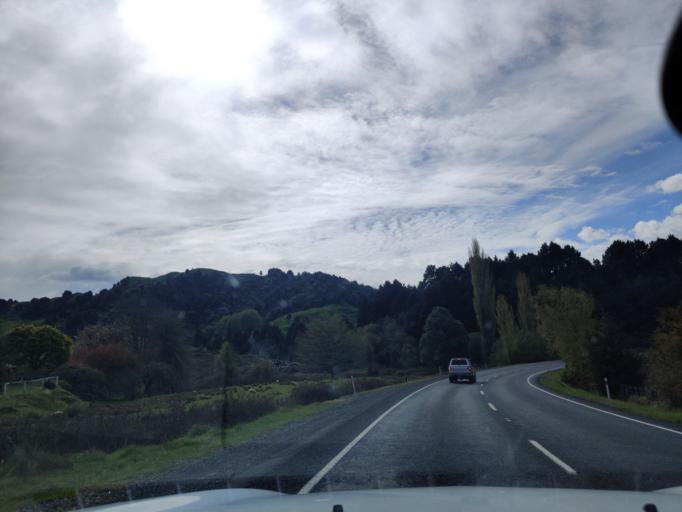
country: NZ
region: Waikato
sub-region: Otorohanga District
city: Otorohanga
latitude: -38.5865
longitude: 175.2158
